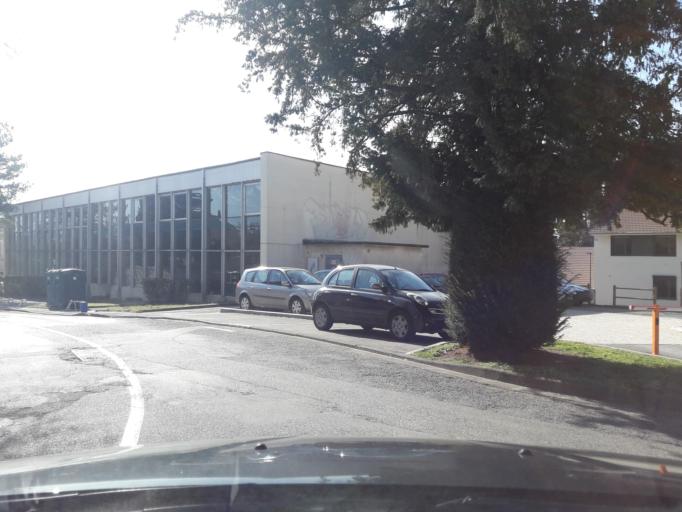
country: FR
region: Rhone-Alpes
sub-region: Departement de l'Isere
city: La Tronche
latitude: 45.2052
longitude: 5.7438
